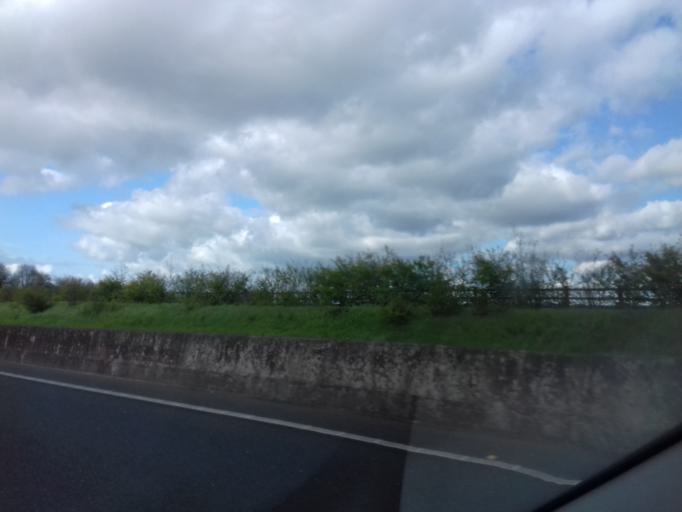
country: IE
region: Leinster
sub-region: Kilkenny
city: Thomastown
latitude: 52.4413
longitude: -7.2352
